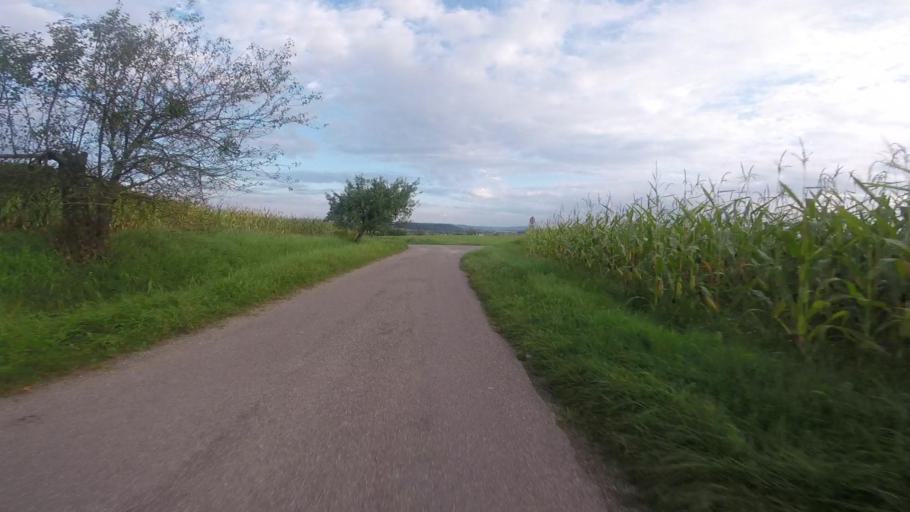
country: DE
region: Baden-Wuerttemberg
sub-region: Regierungsbezirk Stuttgart
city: Oberstenfeld
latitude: 49.0024
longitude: 9.3585
